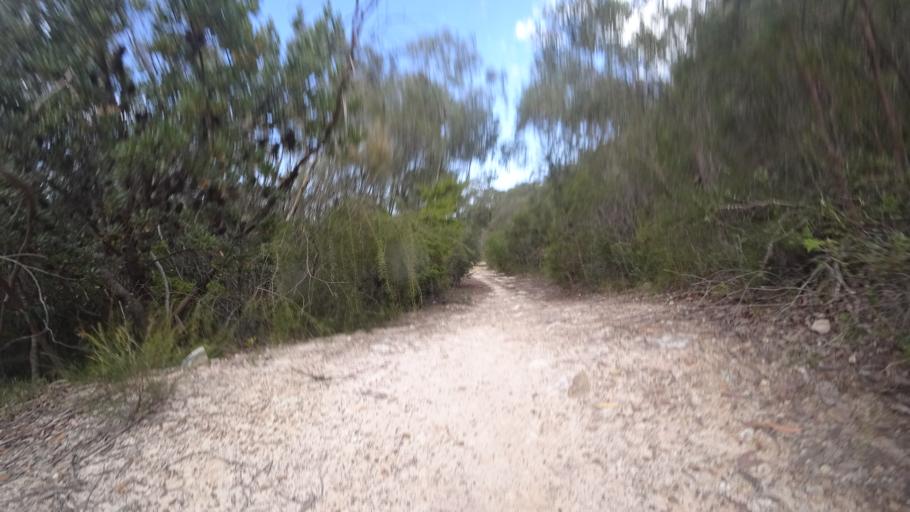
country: AU
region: New South Wales
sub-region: City of Sydney
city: North Turramurra
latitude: -33.6841
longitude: 151.1965
